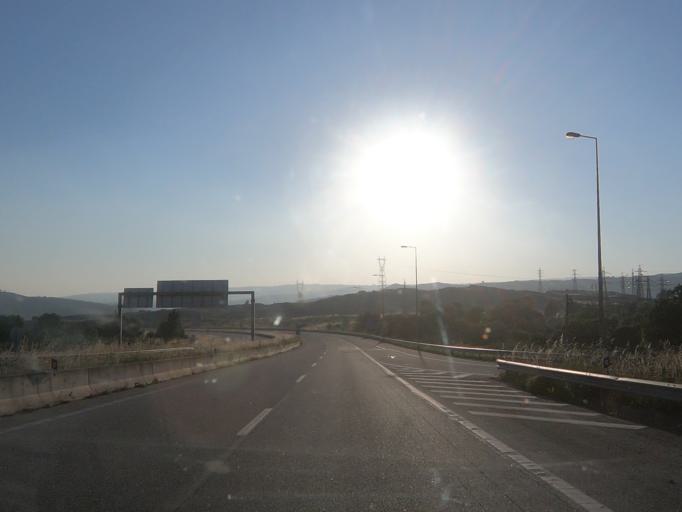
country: PT
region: Guarda
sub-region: Celorico da Beira
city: Celorico da Beira
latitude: 40.6305
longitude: -7.4147
